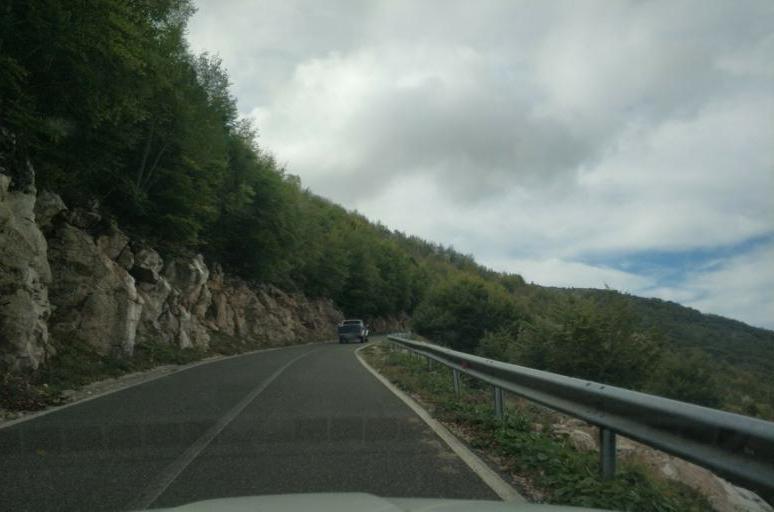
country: AL
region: Durres
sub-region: Rrethi i Krujes
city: Kruje
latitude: 41.5232
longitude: 19.8077
